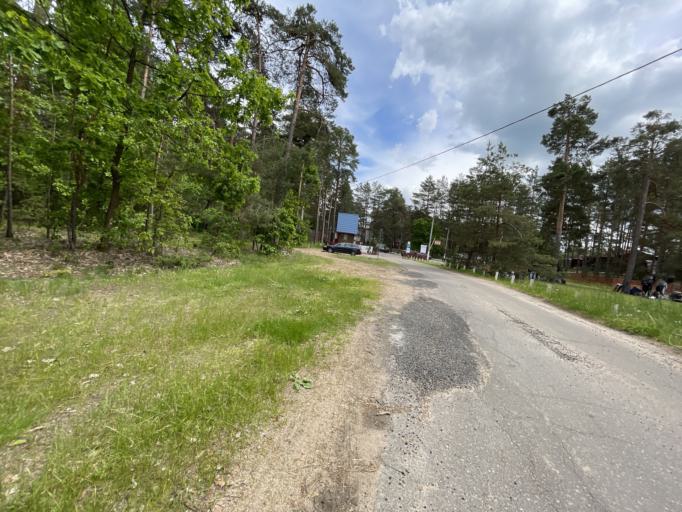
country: BY
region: Minsk
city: Stowbtsy
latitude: 53.4262
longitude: 26.8133
